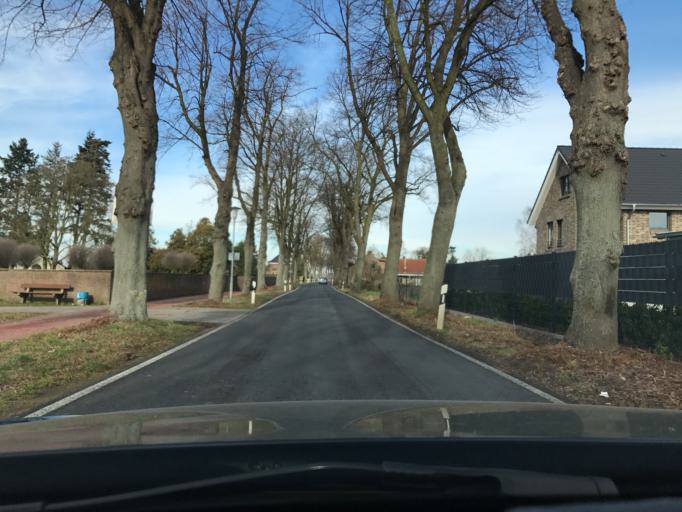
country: DE
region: North Rhine-Westphalia
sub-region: Regierungsbezirk Dusseldorf
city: Grefrath
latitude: 51.3466
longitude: 6.3643
